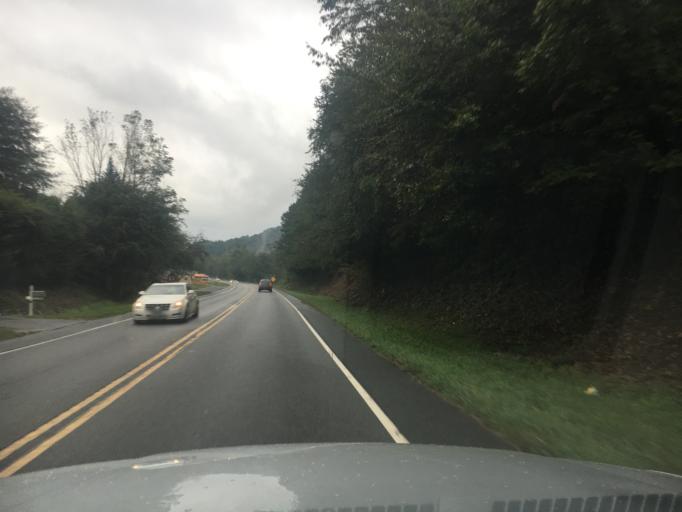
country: US
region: North Carolina
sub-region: Henderson County
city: Etowah
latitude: 35.3222
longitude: -82.5808
